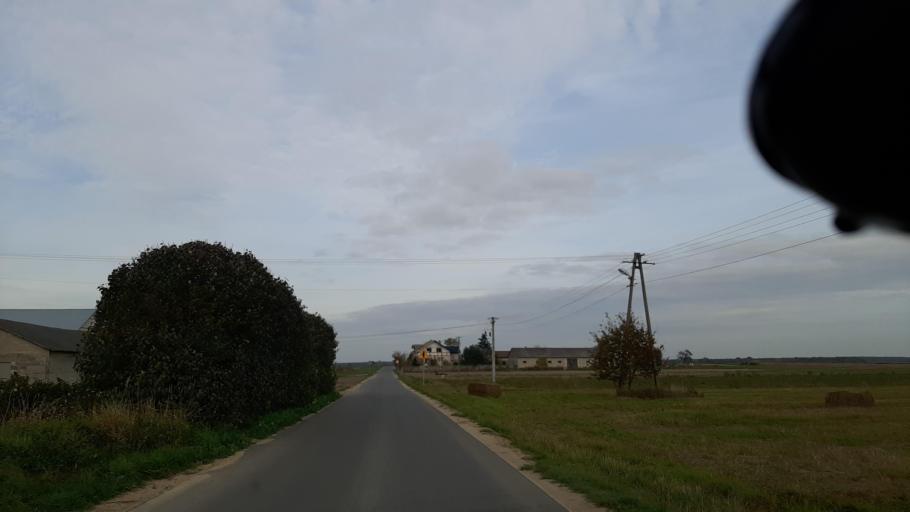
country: PL
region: Lublin Voivodeship
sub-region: Powiat lubelski
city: Garbow
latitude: 51.3864
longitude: 22.3414
